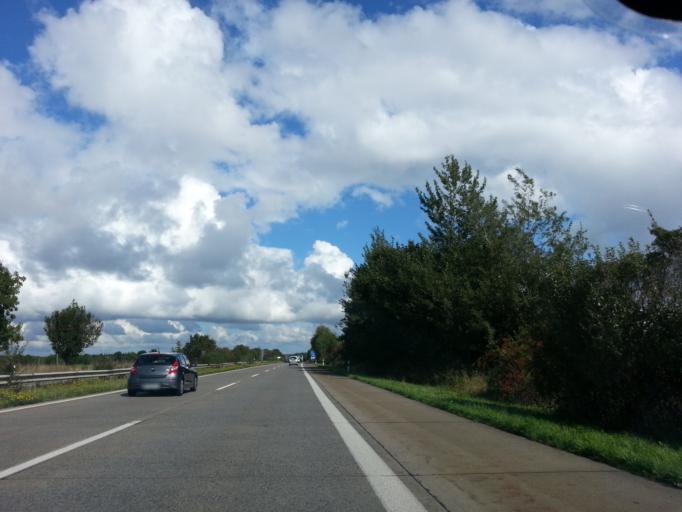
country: DE
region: Schleswig-Holstein
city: Scharbeutz
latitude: 54.0142
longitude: 10.7294
